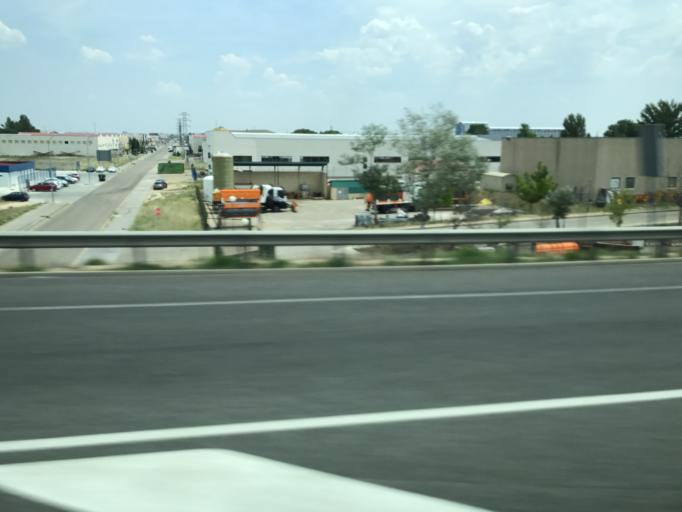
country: ES
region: Castille and Leon
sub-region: Provincia de Burgos
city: Villalba de Duero
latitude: 41.6657
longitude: -3.7283
